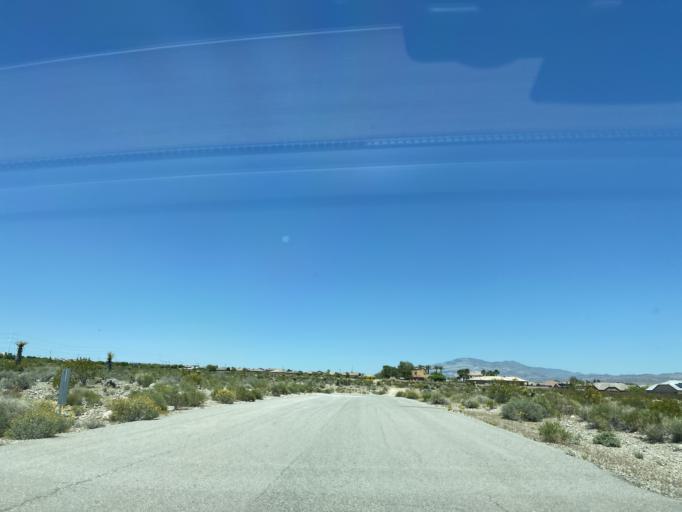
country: US
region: Nevada
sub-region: Clark County
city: Summerlin South
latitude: 36.2819
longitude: -115.3241
